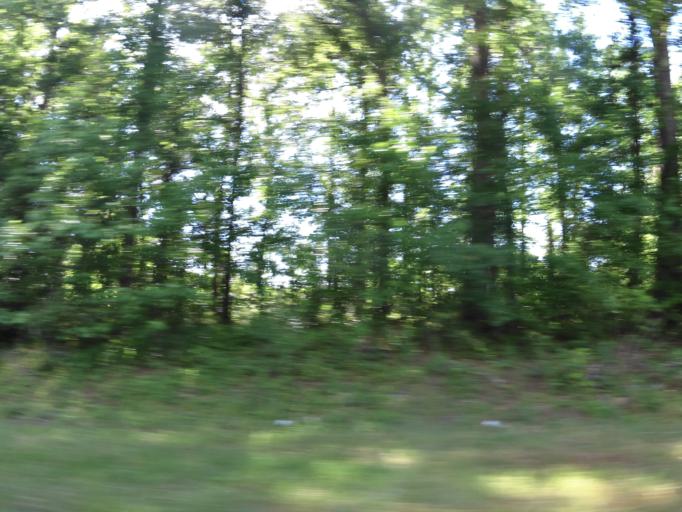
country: US
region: South Carolina
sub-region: Allendale County
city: Fairfax
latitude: 33.0515
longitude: -81.2183
